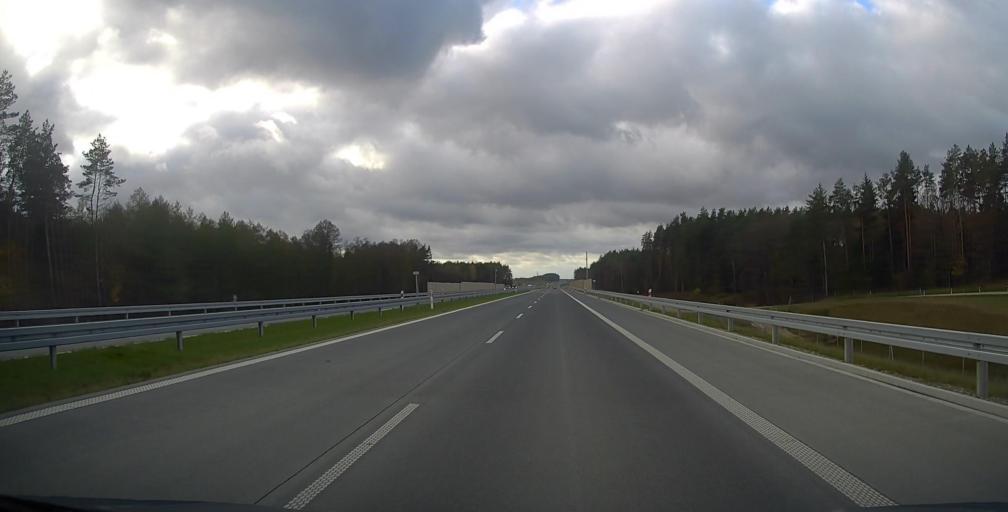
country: PL
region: Podlasie
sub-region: Powiat grajewski
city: Rajgrod
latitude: 53.8710
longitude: 22.6370
